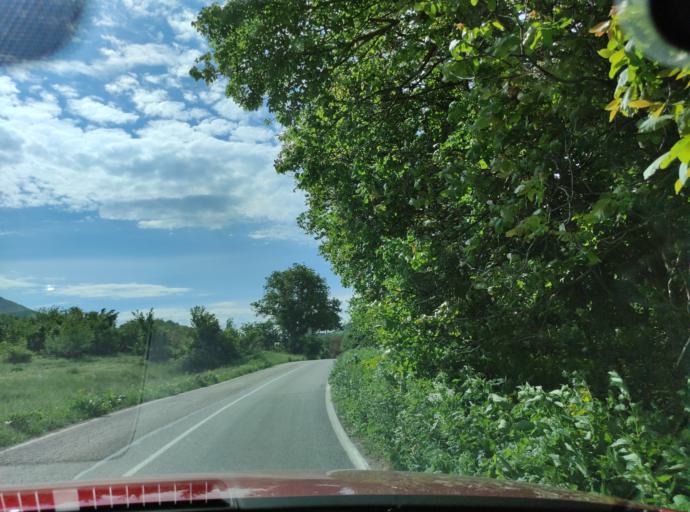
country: BG
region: Montana
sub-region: Obshtina Chiprovtsi
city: Chiprovtsi
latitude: 43.4901
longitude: 22.8098
